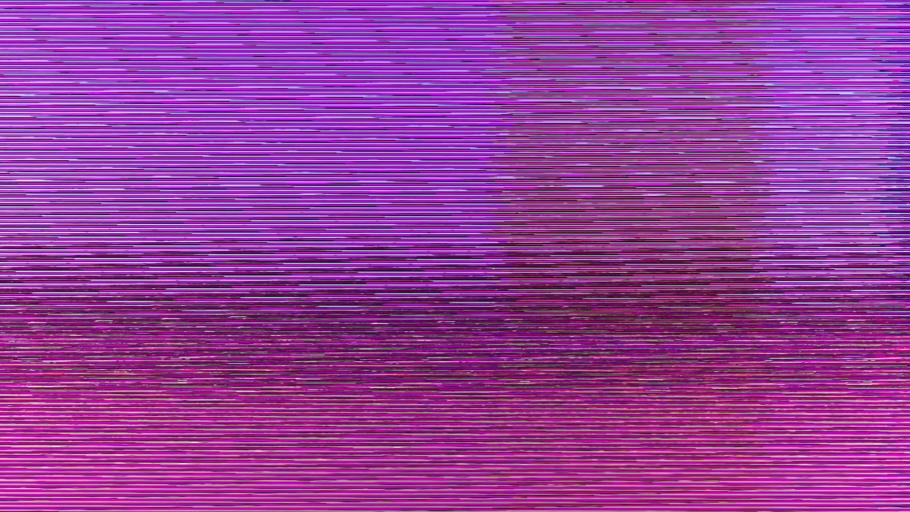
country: US
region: Michigan
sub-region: Oakland County
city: Waterford
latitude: 42.6789
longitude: -83.3690
